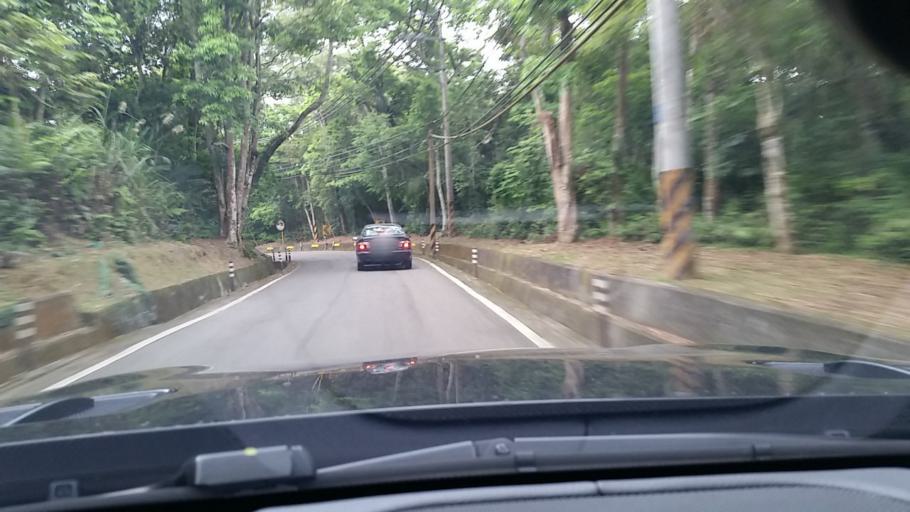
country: TW
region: Taiwan
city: Daxi
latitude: 24.8038
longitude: 121.2954
